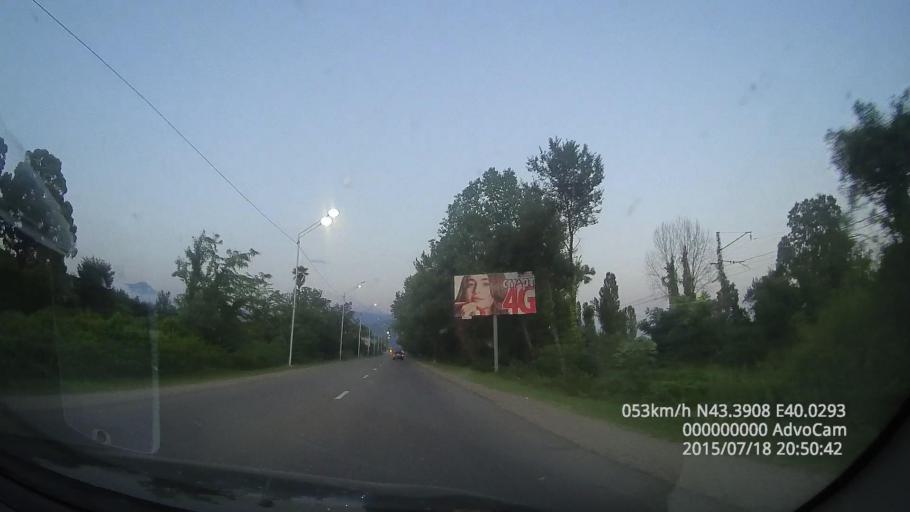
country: GE
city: Gantiadi
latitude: 43.3906
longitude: 40.0307
